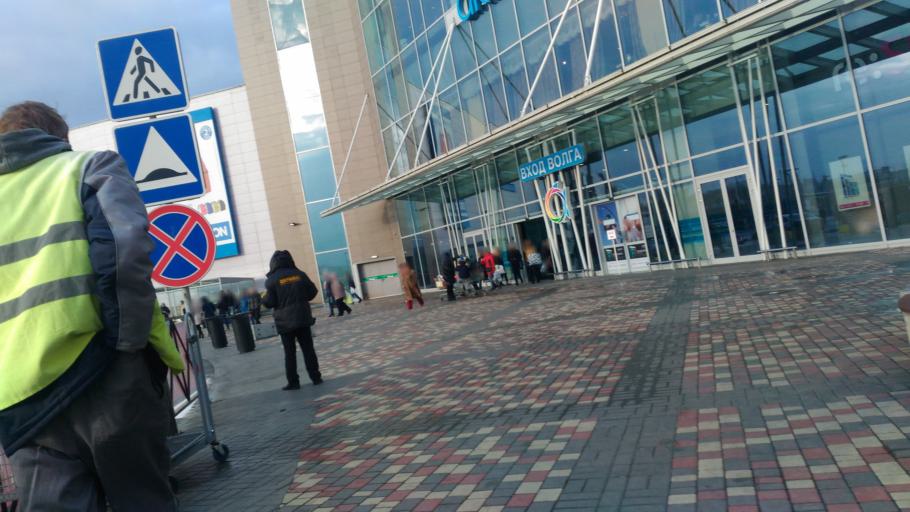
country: RU
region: Volgograd
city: Volgograd
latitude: 48.6370
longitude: 44.4350
